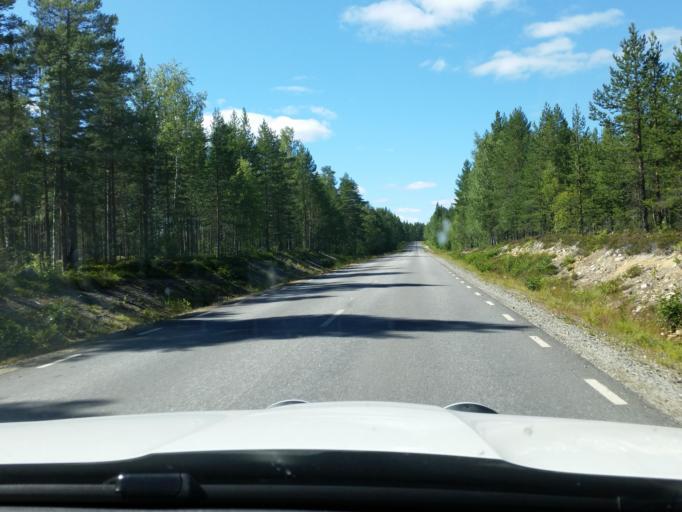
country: SE
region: Norrbotten
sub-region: Pitea Kommun
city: Roknas
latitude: 65.2052
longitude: 21.1952
